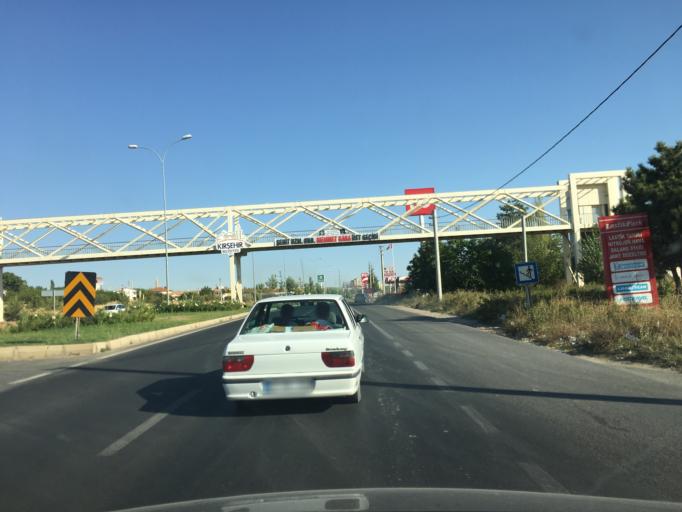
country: TR
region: Kirsehir
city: Kirsehir
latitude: 39.1338
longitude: 34.1863
